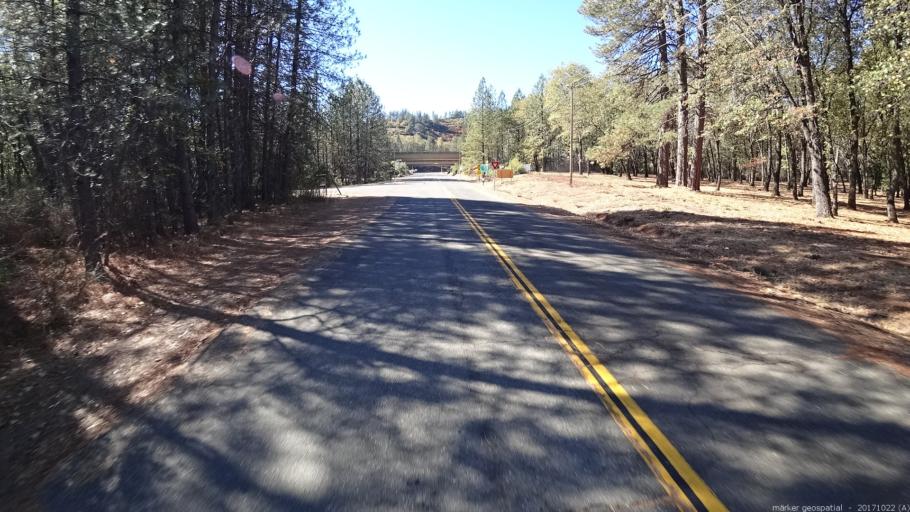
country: US
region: California
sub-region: Shasta County
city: Central Valley (historical)
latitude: 40.9114
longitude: -122.3838
